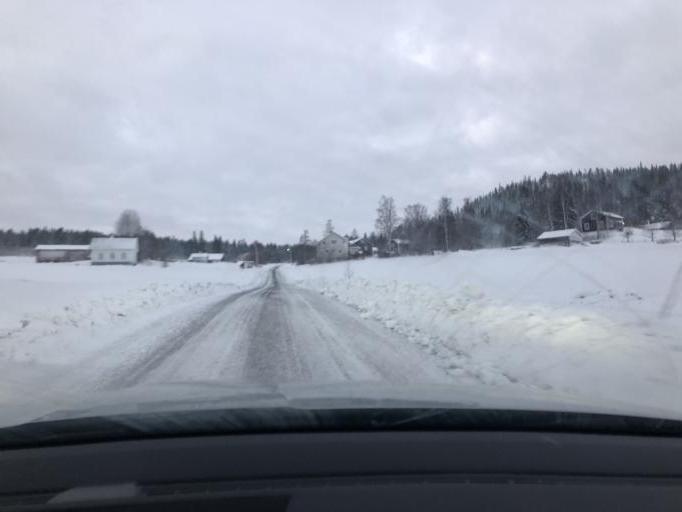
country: SE
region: Vaesternorrland
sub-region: Kramfors Kommun
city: Nordingra
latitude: 62.9127
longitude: 18.2345
